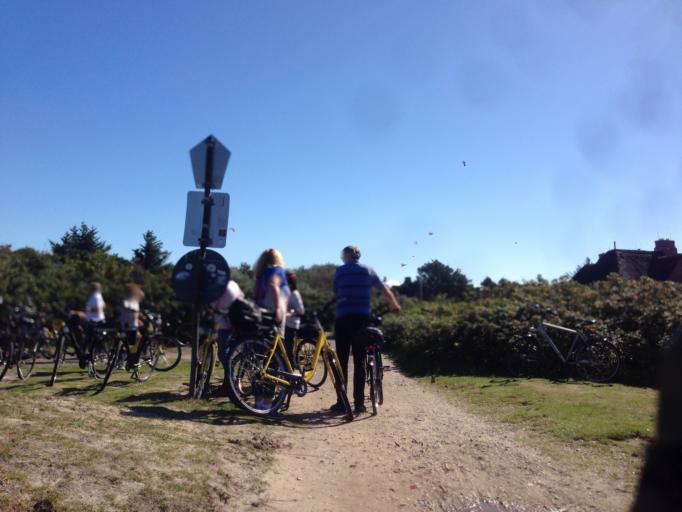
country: DE
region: Schleswig-Holstein
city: Tinnum
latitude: 54.9545
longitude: 8.3372
